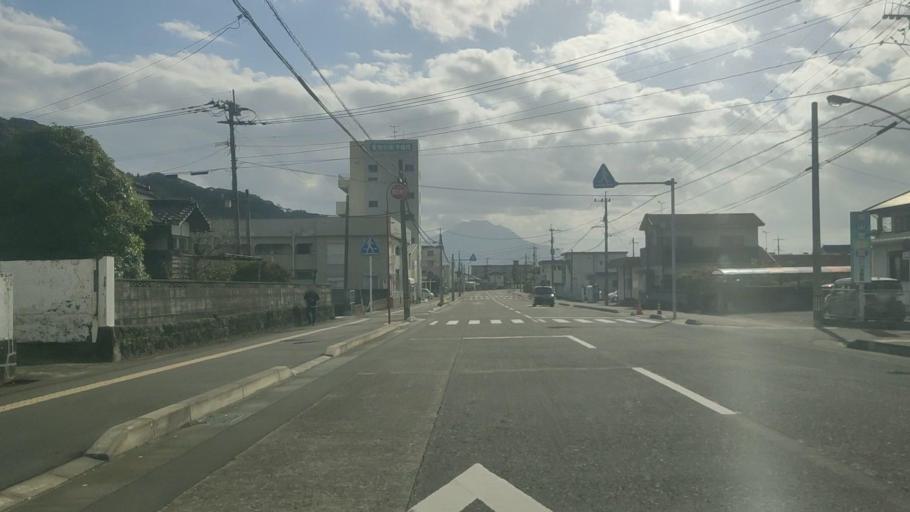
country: JP
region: Kagoshima
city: Kajiki
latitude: 31.7379
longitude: 130.6703
